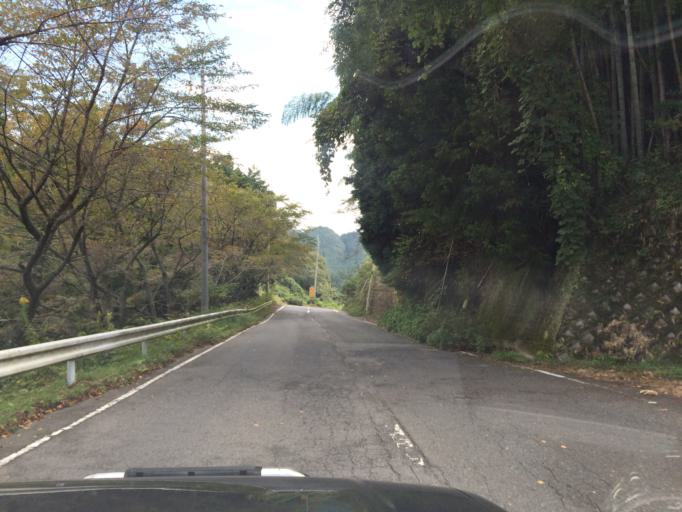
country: JP
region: Mie
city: Nabari
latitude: 34.6790
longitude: 135.9678
